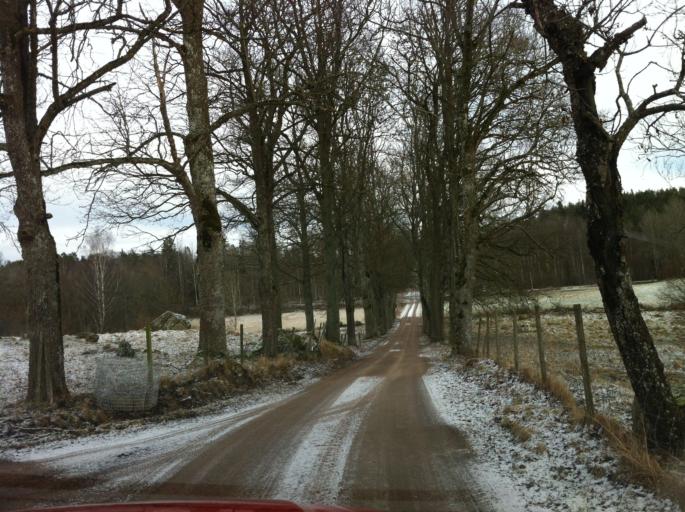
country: SE
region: Joenkoeping
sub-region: Eksjo Kommun
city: Mariannelund
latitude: 57.6161
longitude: 15.7095
